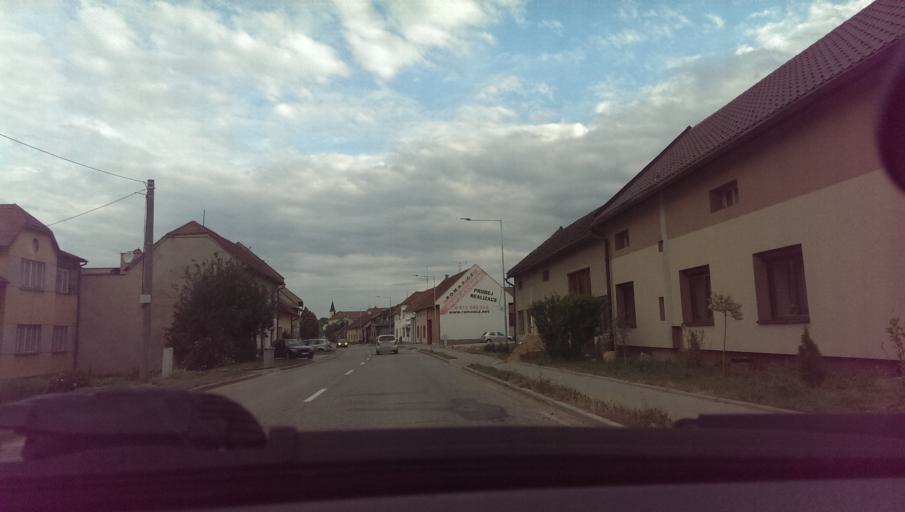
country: CZ
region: Zlin
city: Topolna
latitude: 49.1174
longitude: 17.5441
